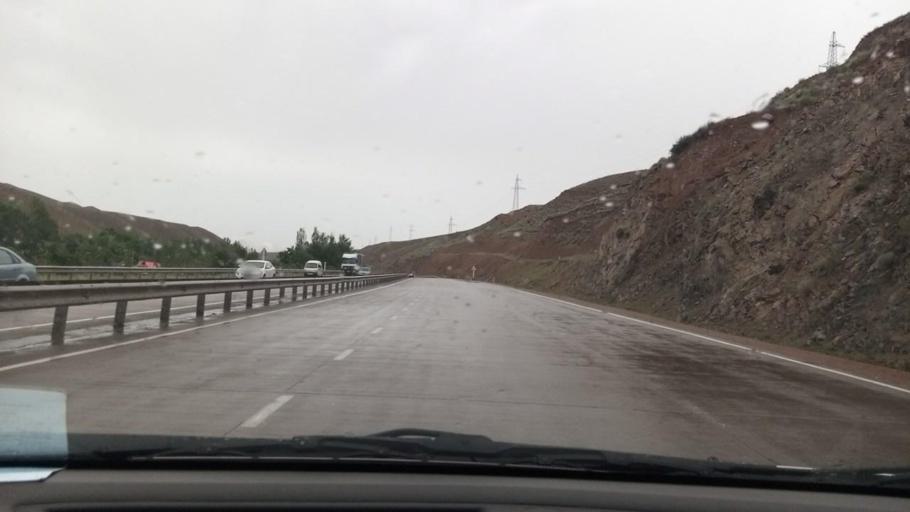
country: TJ
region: Viloyati Sughd
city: Shaydon
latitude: 40.9533
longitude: 70.6750
